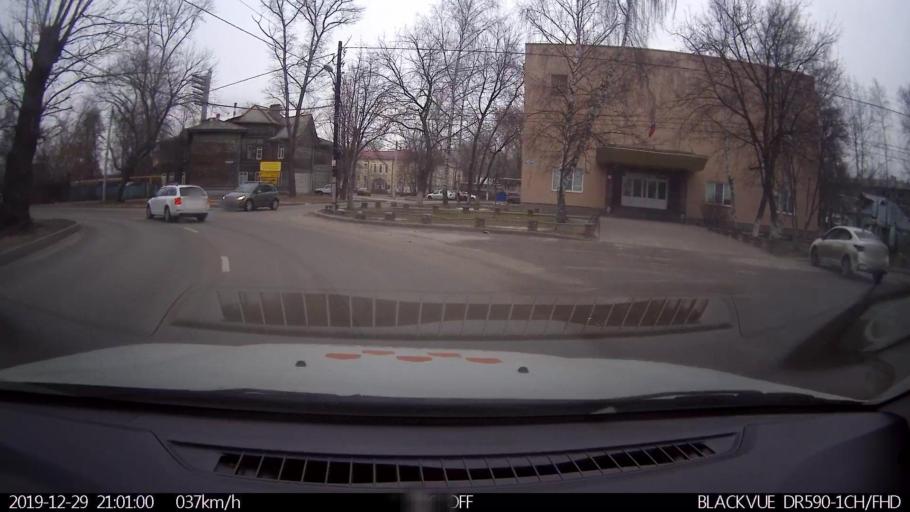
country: RU
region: Nizjnij Novgorod
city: Nizhniy Novgorod
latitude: 56.3067
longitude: 43.9301
